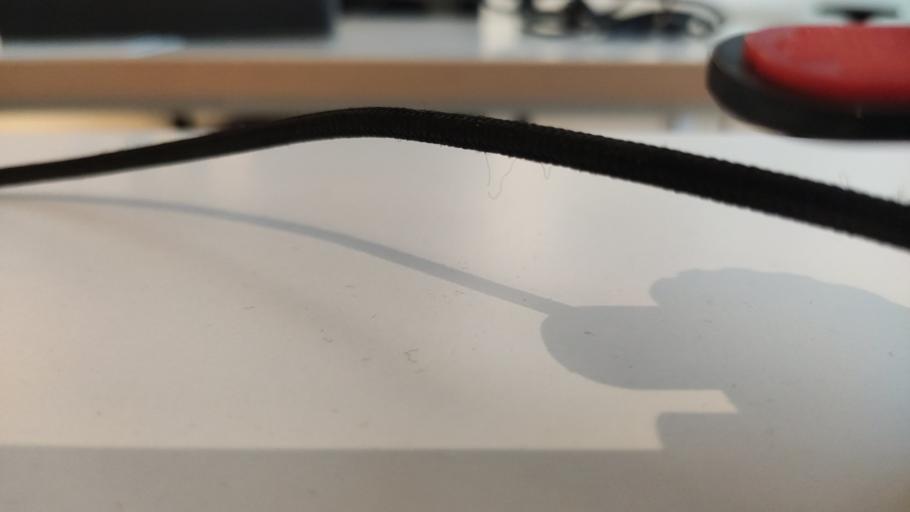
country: RU
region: Moskovskaya
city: Novopetrovskoye
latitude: 55.9326
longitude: 36.4342
